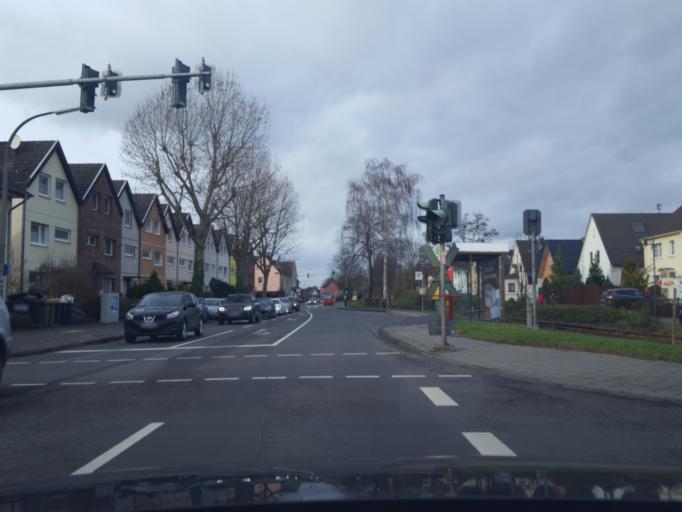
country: DE
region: North Rhine-Westphalia
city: Niederkassel
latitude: 50.7914
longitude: 7.0537
